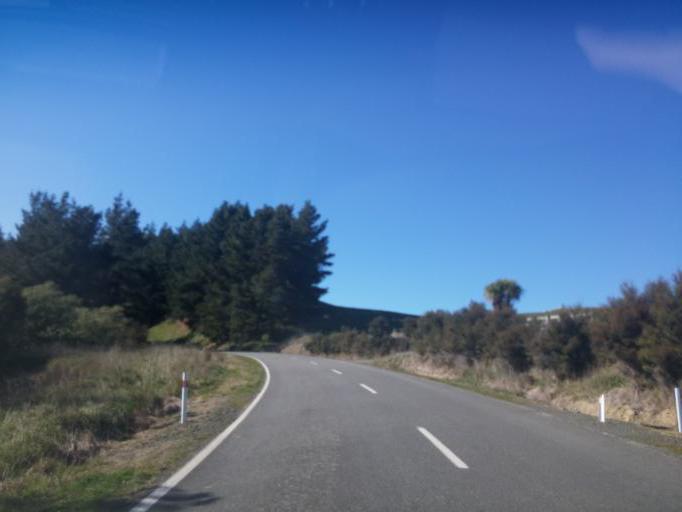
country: NZ
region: Wellington
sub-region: South Wairarapa District
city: Waipawa
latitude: -41.3491
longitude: 175.4849
